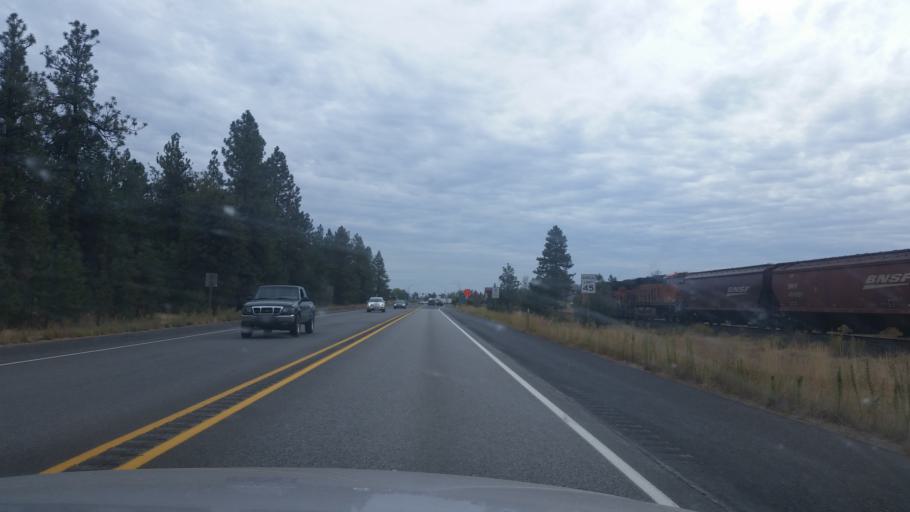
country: US
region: Washington
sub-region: Spokane County
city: Cheney
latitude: 47.5118
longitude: -117.5647
